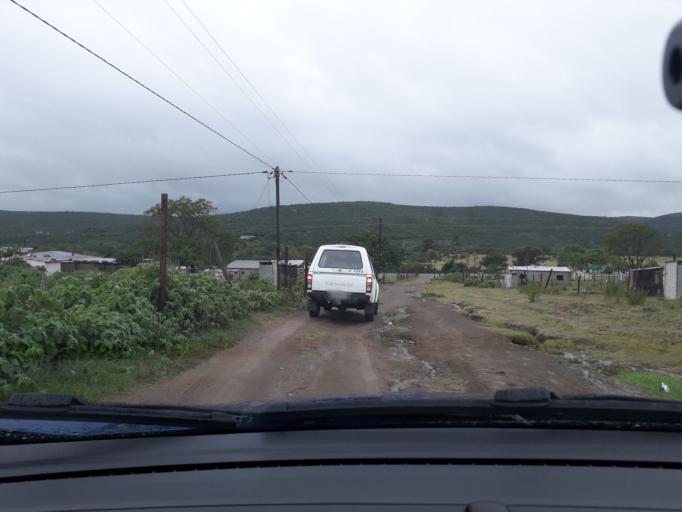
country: ZA
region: Eastern Cape
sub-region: Buffalo City Metropolitan Municipality
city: Bhisho
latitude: -32.8069
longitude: 27.3686
